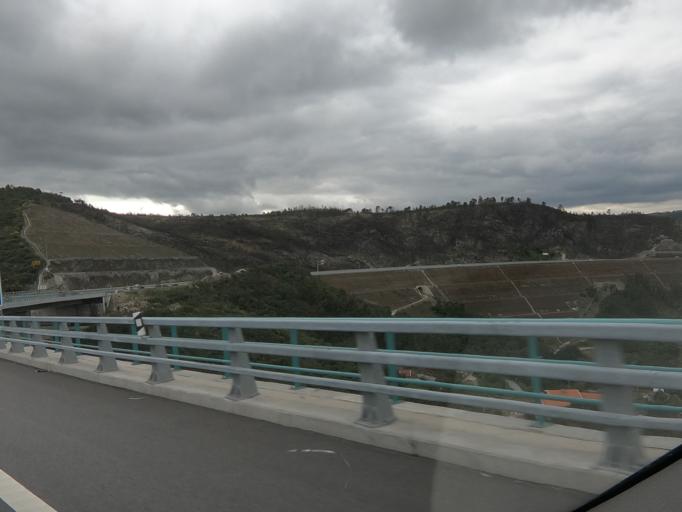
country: PT
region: Porto
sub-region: Amarante
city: Amarante
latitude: 41.2480
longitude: -7.9902
